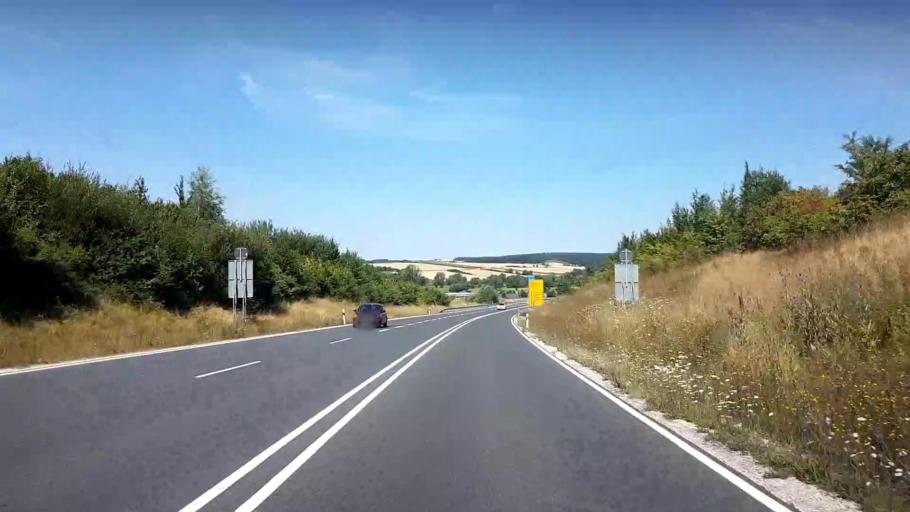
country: DE
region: Bavaria
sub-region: Upper Franconia
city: Grossheirath
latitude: 50.1831
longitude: 10.9628
